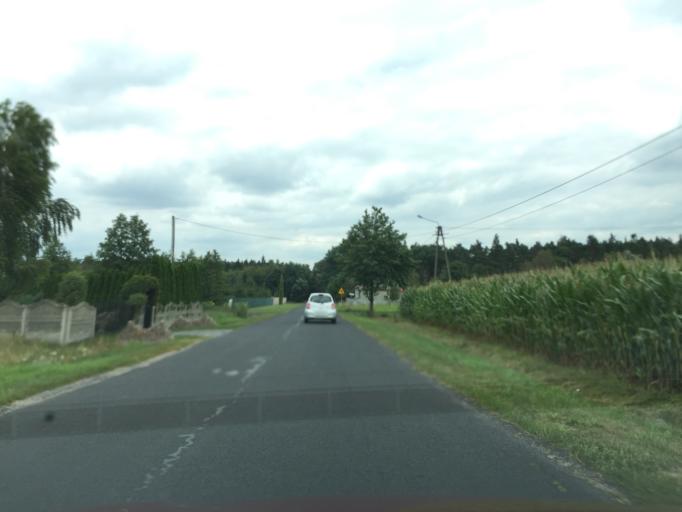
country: PL
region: Greater Poland Voivodeship
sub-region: Powiat kaliski
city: Stawiszyn
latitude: 51.9630
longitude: 18.1781
